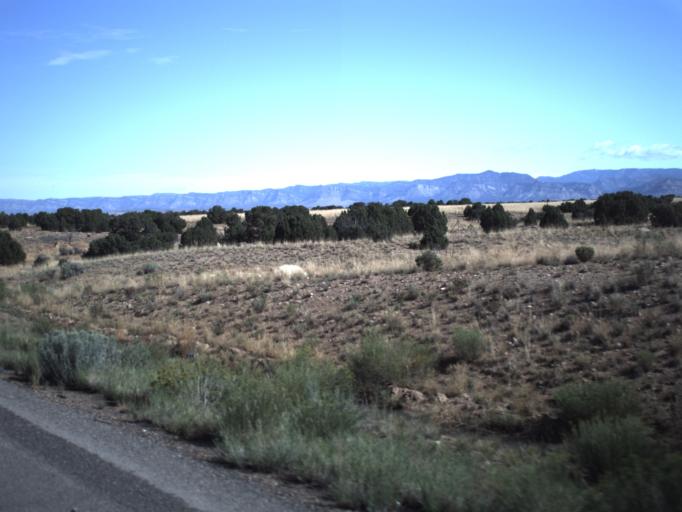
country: US
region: Utah
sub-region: Carbon County
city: East Carbon City
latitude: 39.4164
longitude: -110.4371
